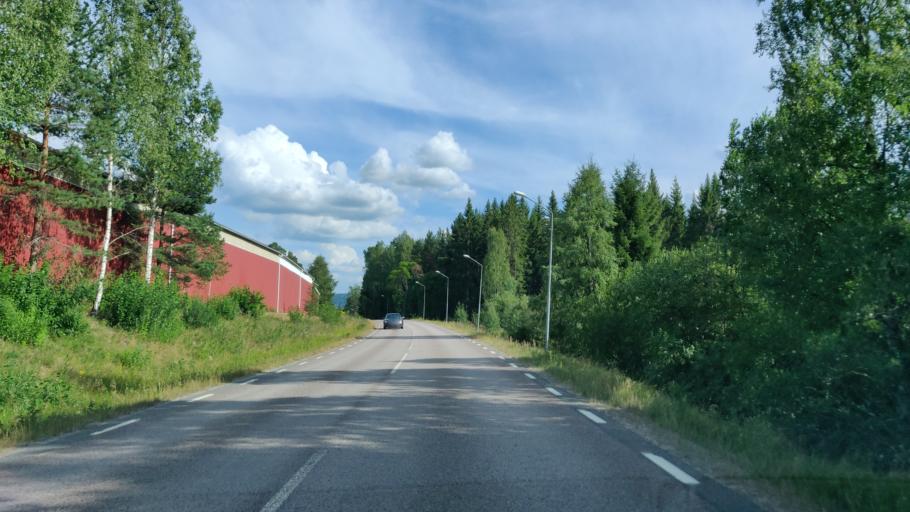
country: SE
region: Vaermland
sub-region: Hagfors Kommun
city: Hagfors
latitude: 60.0692
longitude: 13.6339
